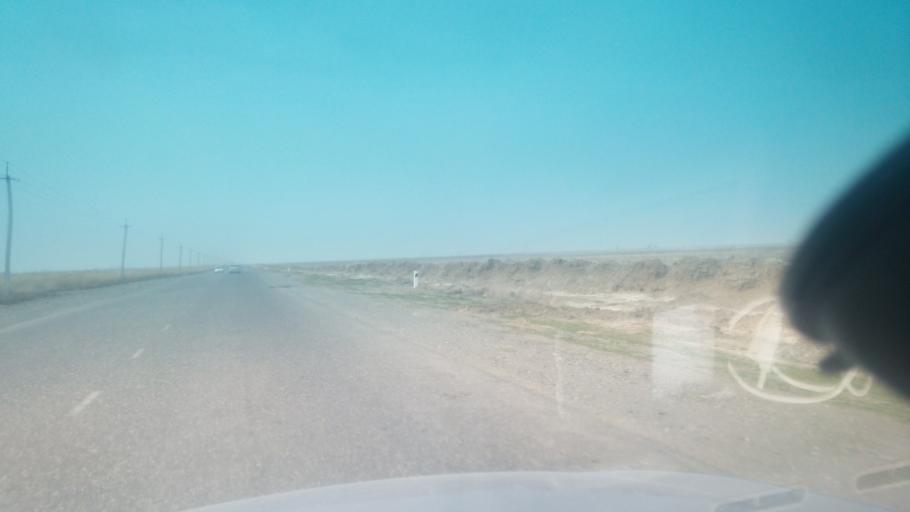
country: TJ
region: Viloyati Sughd
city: Pakhtakoron
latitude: 40.2071
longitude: 68.7770
